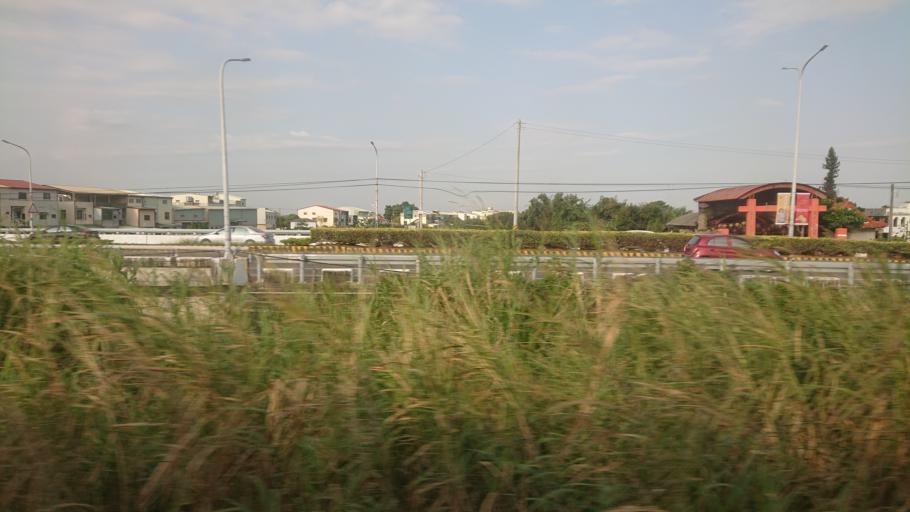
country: TW
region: Taiwan
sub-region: Yunlin
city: Douliu
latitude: 23.6628
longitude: 120.4748
